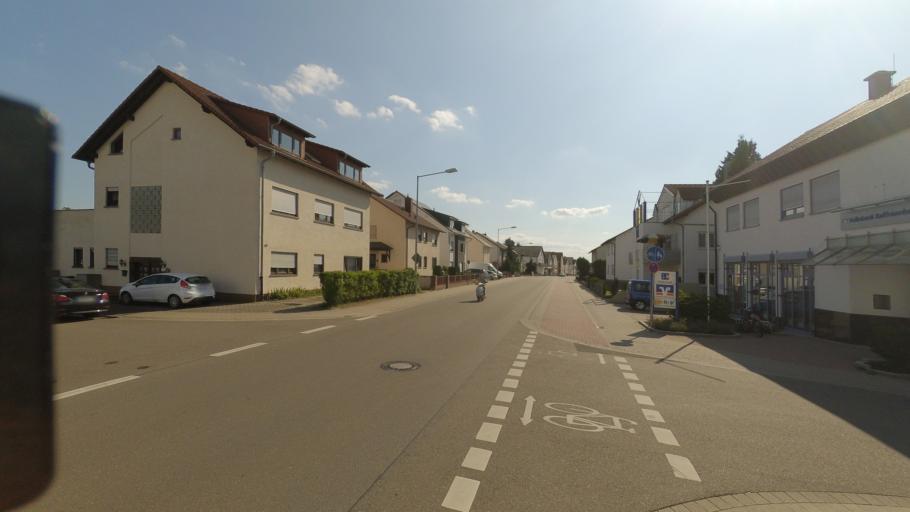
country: DE
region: Rheinland-Pfalz
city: Schifferstadt
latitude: 49.3794
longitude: 8.3835
